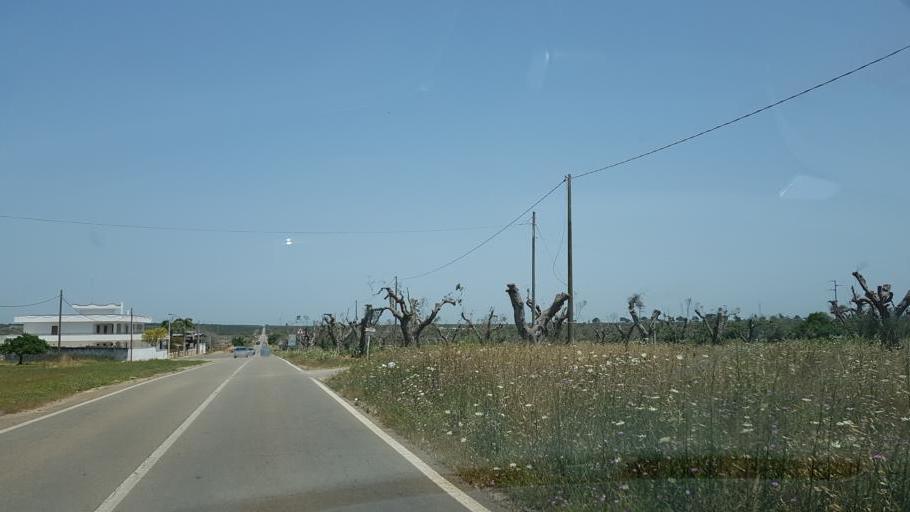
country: IT
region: Apulia
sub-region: Provincia di Lecce
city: Porto Cesareo
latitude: 40.2751
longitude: 17.9023
